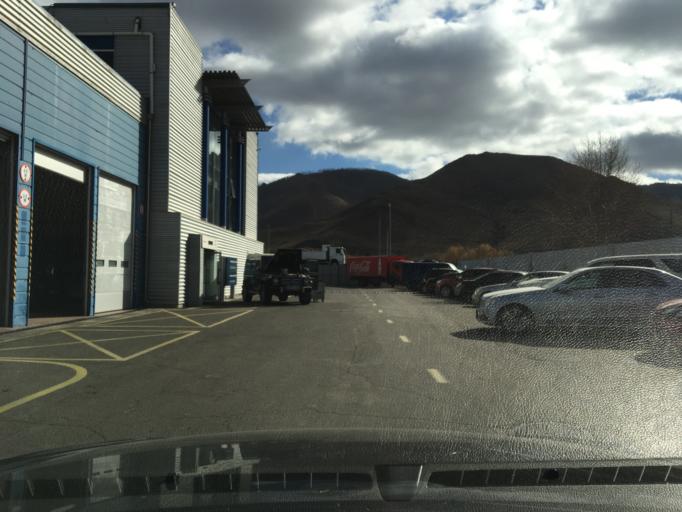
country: MN
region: Ulaanbaatar
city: Ulaanbaatar
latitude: 47.8916
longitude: 106.8685
